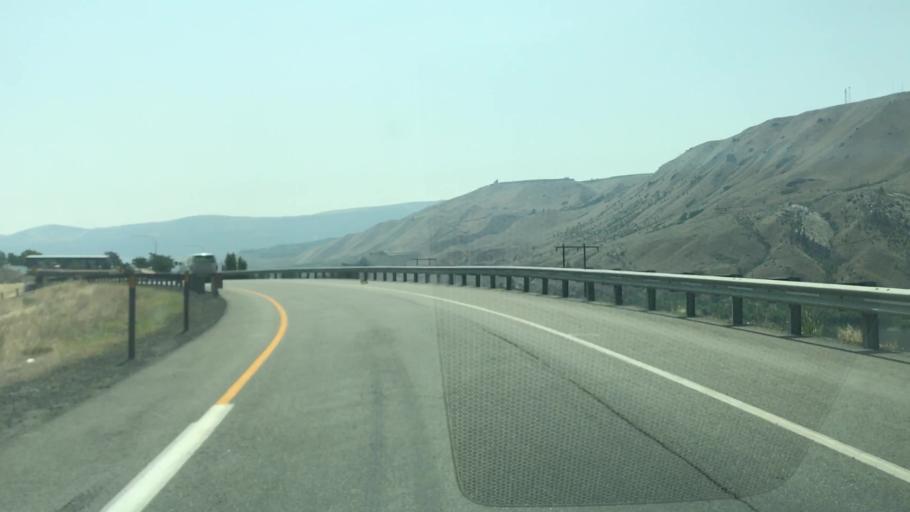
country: US
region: Washington
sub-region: Chelan County
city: South Wenatchee
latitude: 47.3993
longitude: -120.2883
